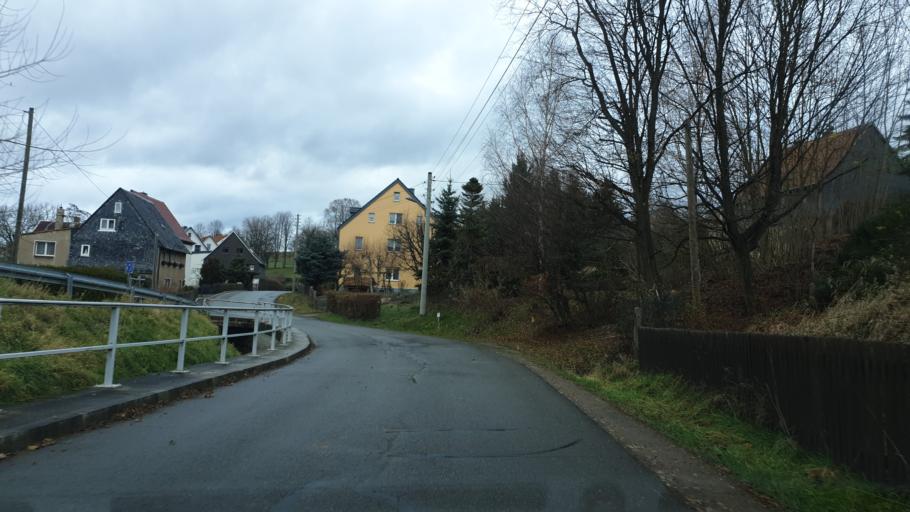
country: DE
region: Saxony
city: Bernsdorf
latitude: 50.7619
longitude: 12.6675
